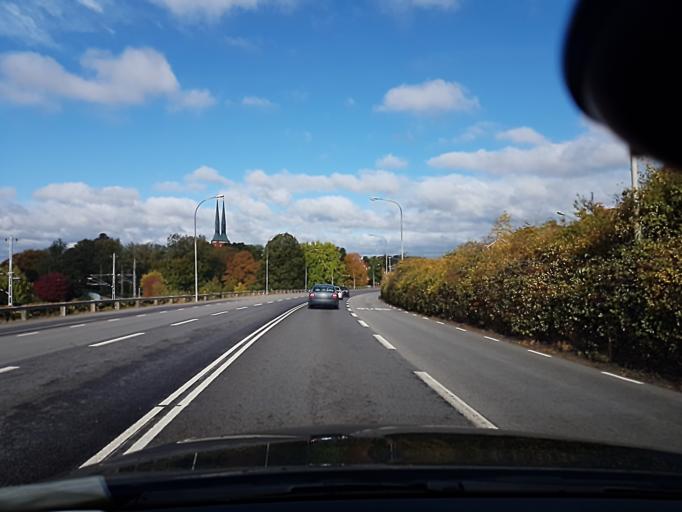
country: SE
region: Kronoberg
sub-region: Vaxjo Kommun
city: Vaexjoe
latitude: 56.8746
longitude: 14.8165
